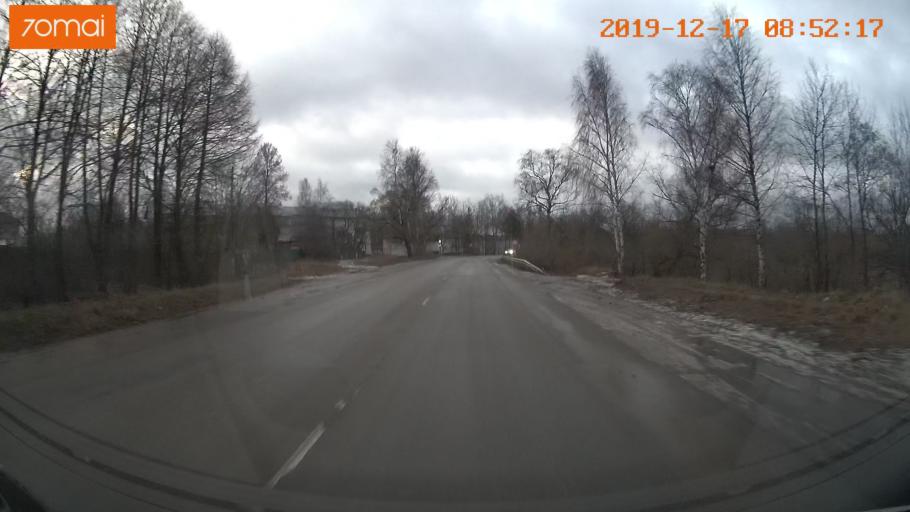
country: RU
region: Vladimir
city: Kosterevo
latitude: 55.9500
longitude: 39.6339
